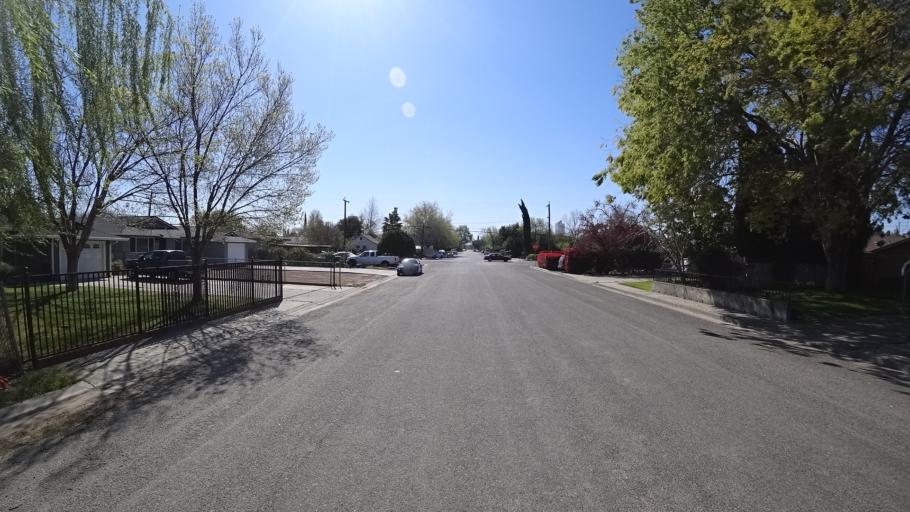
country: US
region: California
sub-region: Glenn County
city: Hamilton City
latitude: 39.7445
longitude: -122.0095
